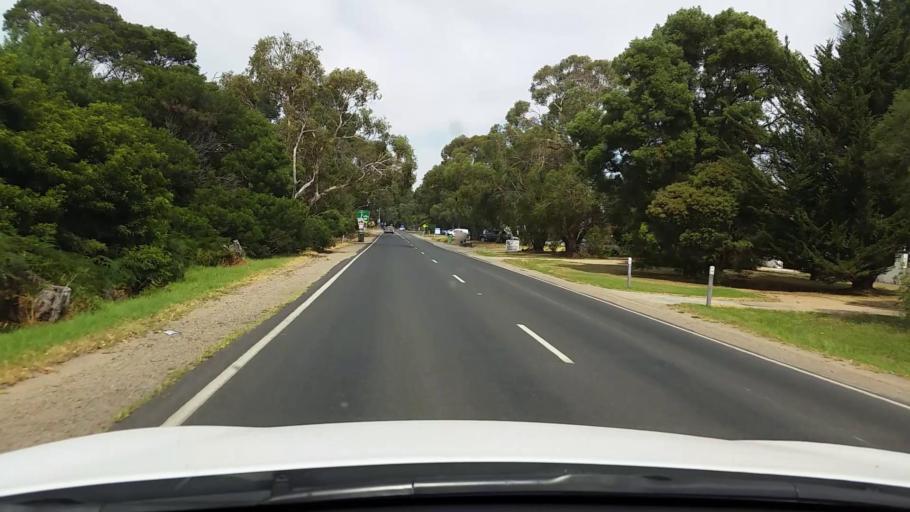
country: AU
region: Victoria
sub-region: Mornington Peninsula
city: Balnarring
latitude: -38.3721
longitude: 145.1295
